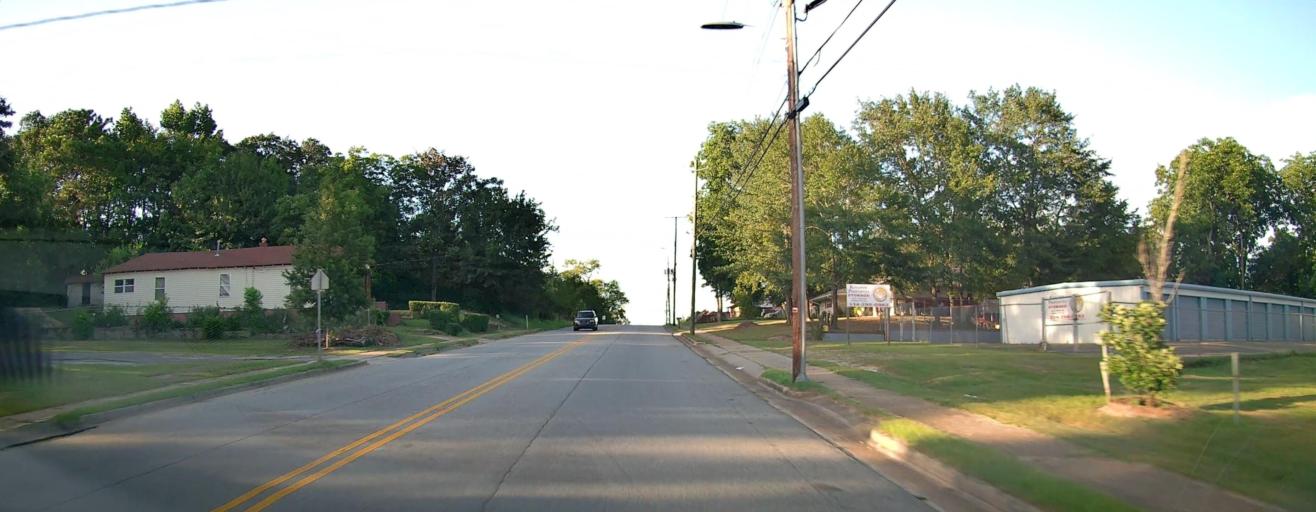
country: US
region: Georgia
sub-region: Muscogee County
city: Columbus
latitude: 32.4448
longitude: -85.0099
